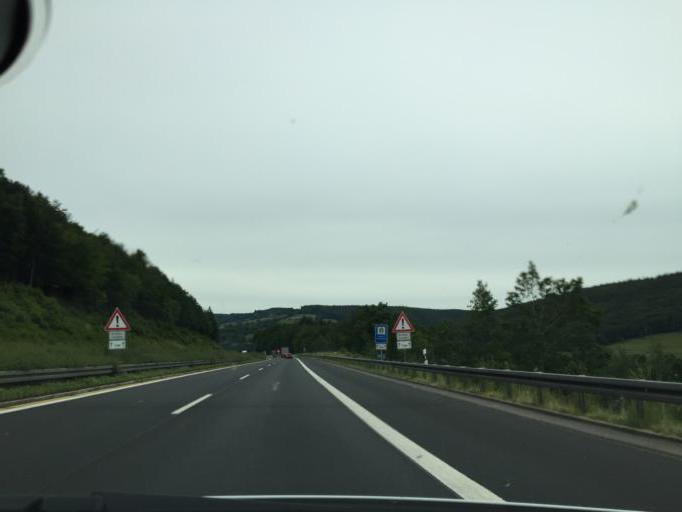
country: DE
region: Bavaria
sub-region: Regierungsbezirk Unterfranken
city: Riedenberg
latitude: 50.3225
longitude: 9.8247
